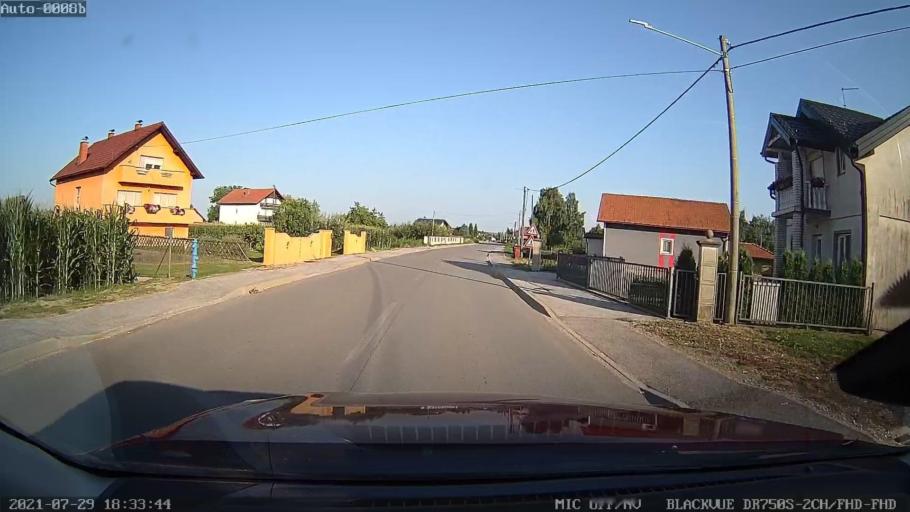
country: HR
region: Varazdinska
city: Vinica
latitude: 46.3141
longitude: 16.1598
